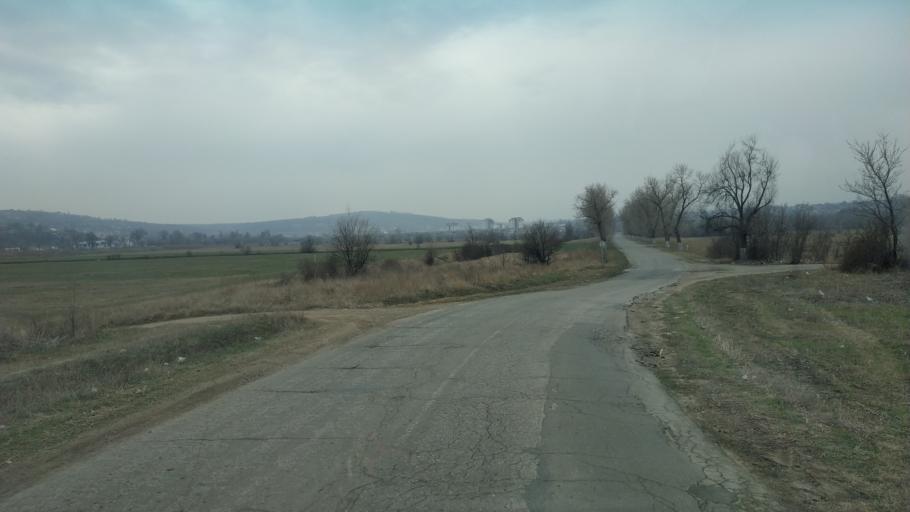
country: MD
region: Chisinau
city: Singera
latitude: 46.9286
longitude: 28.9829
